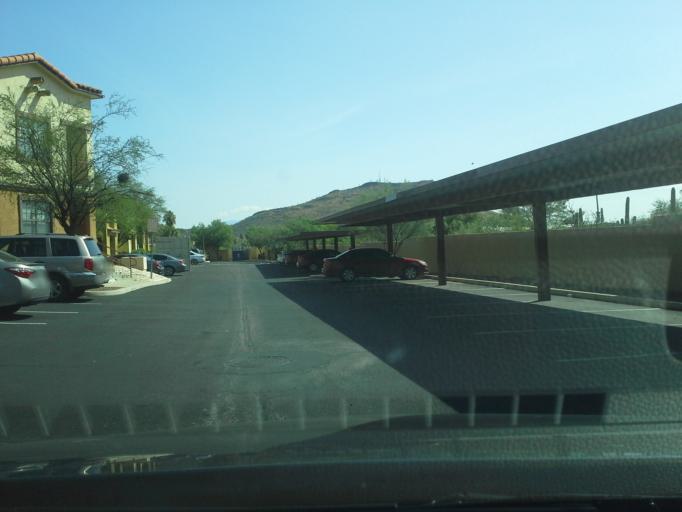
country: US
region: Arizona
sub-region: Pima County
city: South Tucson
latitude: 32.2181
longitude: -111.0274
